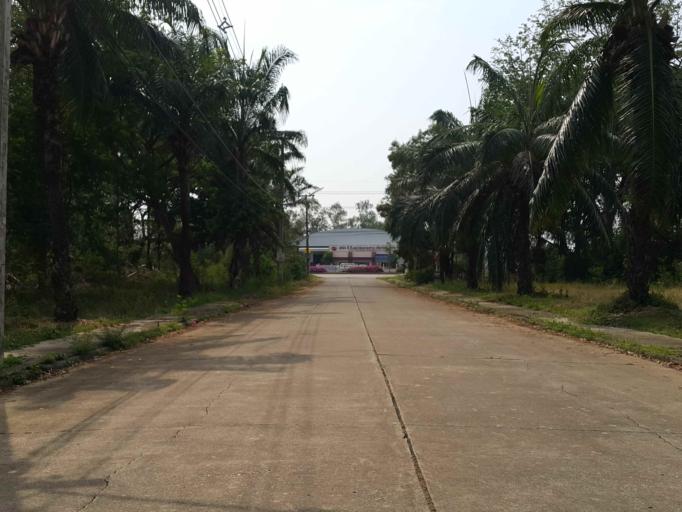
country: TH
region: Chiang Mai
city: San Kamphaeng
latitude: 18.7592
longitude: 99.0761
